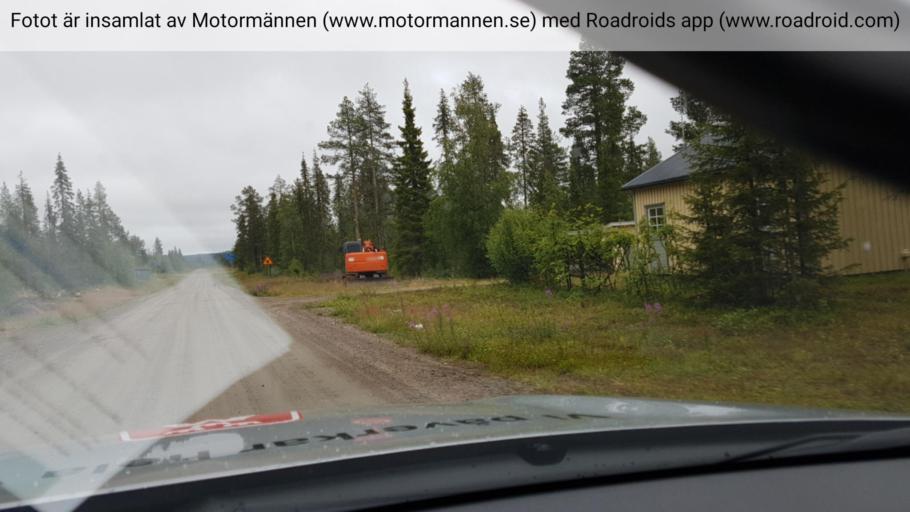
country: SE
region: Norrbotten
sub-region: Gallivare Kommun
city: Gaellivare
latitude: 66.7065
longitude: 20.4475
